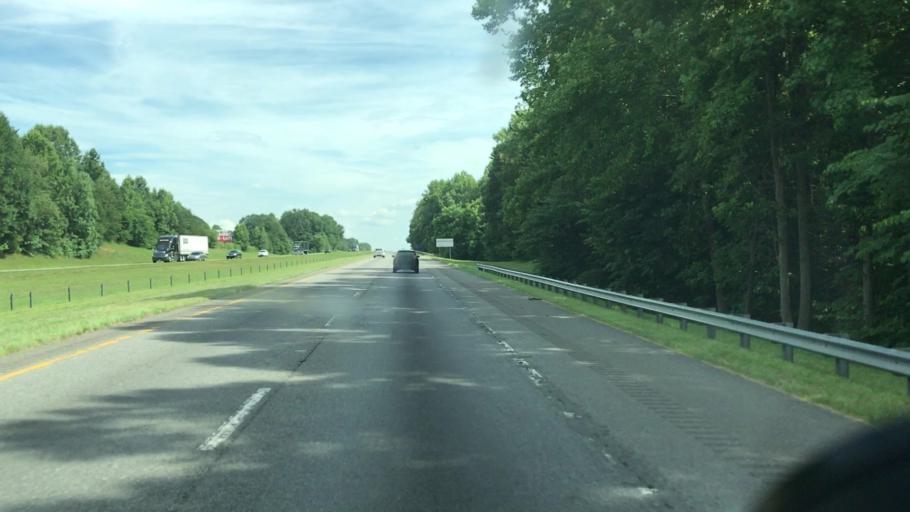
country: US
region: North Carolina
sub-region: Iredell County
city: Statesville
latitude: 35.8785
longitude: -80.8667
